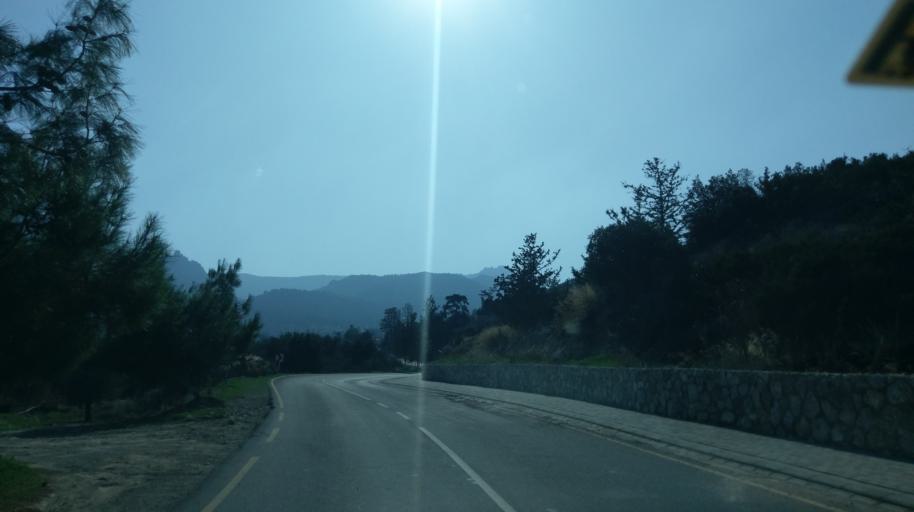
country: CY
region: Ammochostos
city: Lefkonoiko
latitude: 35.3839
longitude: 33.7518
